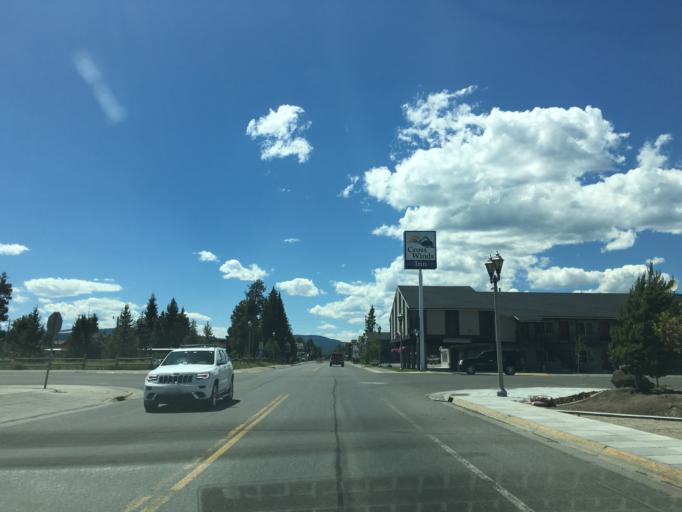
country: US
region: Montana
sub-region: Gallatin County
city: West Yellowstone
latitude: 44.6622
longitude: -111.1015
